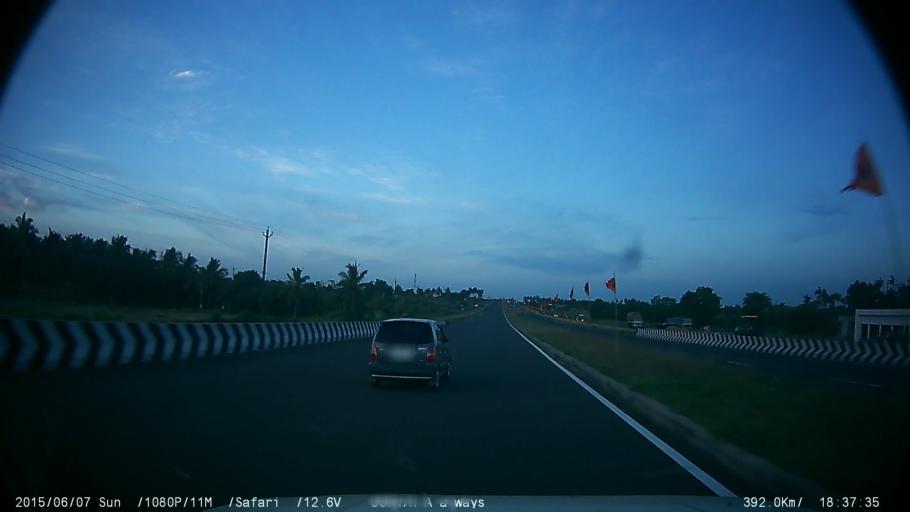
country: IN
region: Tamil Nadu
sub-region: Tiruppur
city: Avinashi
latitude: 11.1997
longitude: 77.3196
